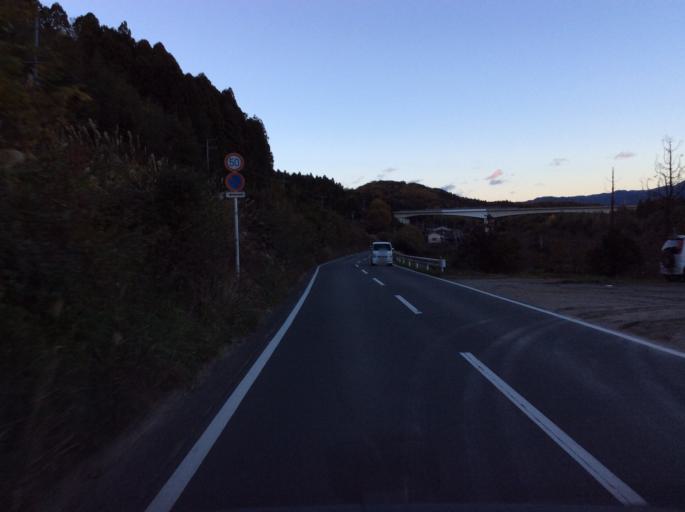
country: JP
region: Fukushima
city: Iwaki
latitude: 37.0917
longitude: 140.8615
